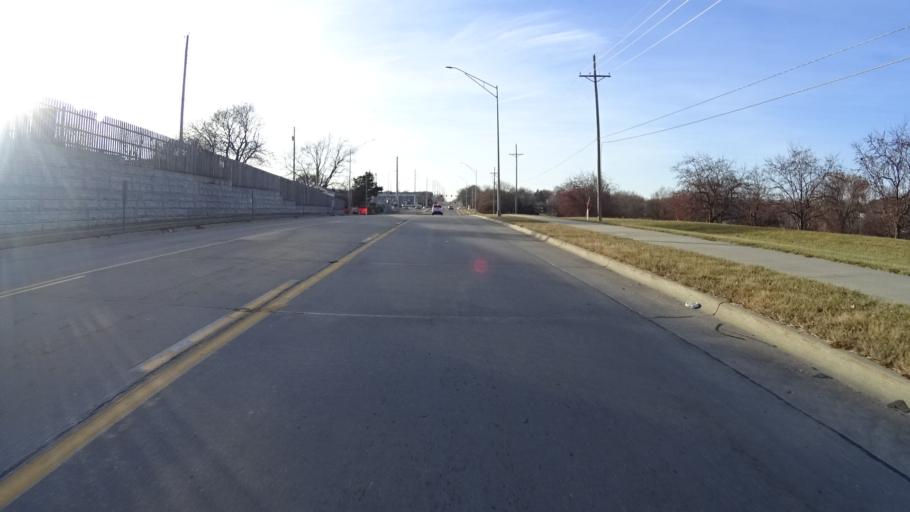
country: US
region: Nebraska
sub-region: Sarpy County
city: La Vista
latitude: 41.1908
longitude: -96.0206
